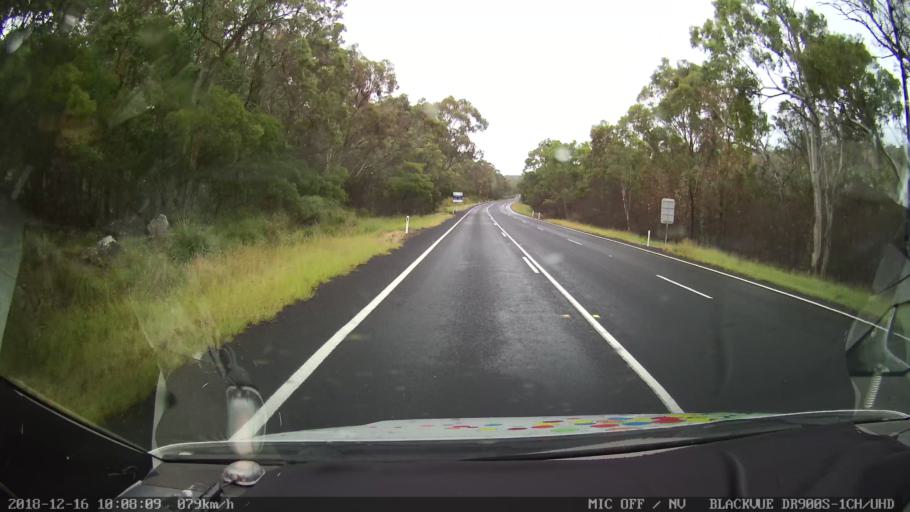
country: AU
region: New South Wales
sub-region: Glen Innes Severn
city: Glen Innes
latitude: -29.3315
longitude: 151.9026
